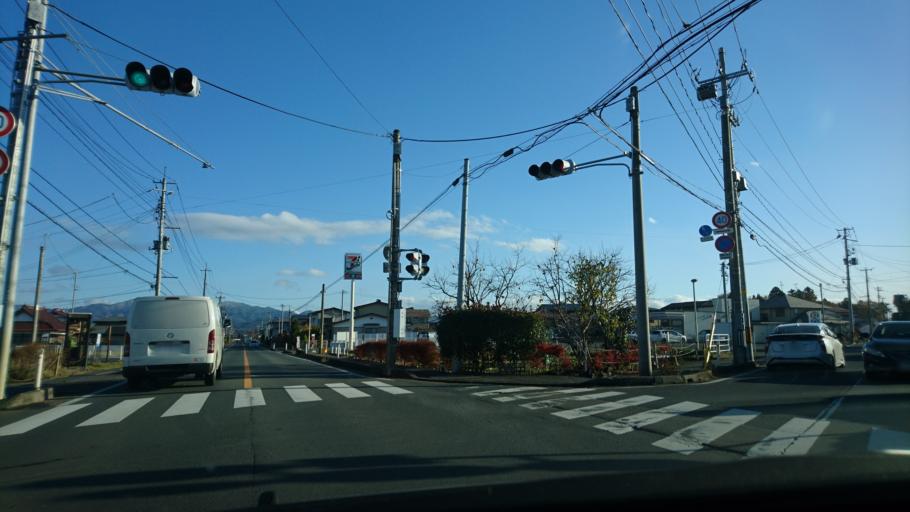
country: JP
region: Iwate
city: Mizusawa
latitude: 39.1293
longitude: 141.1562
